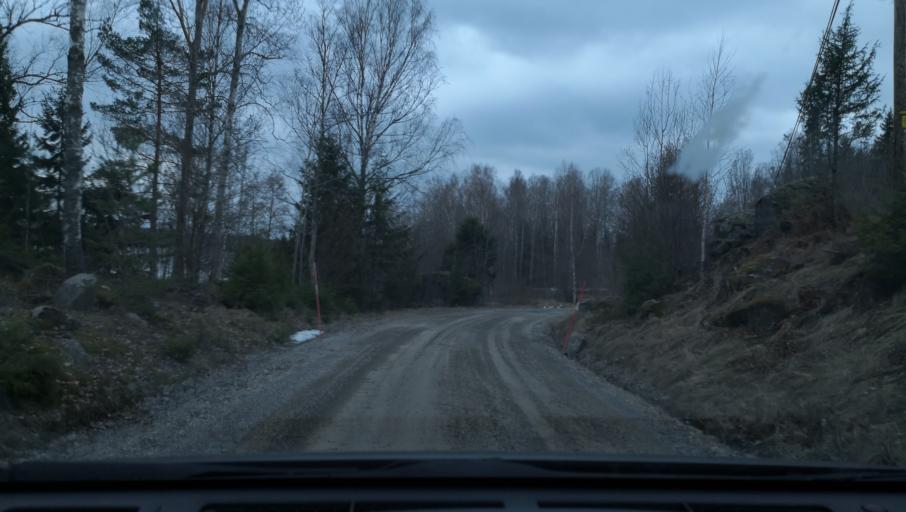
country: SE
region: OErebro
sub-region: Lindesbergs Kommun
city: Fellingsbro
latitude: 59.5986
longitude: 15.6331
